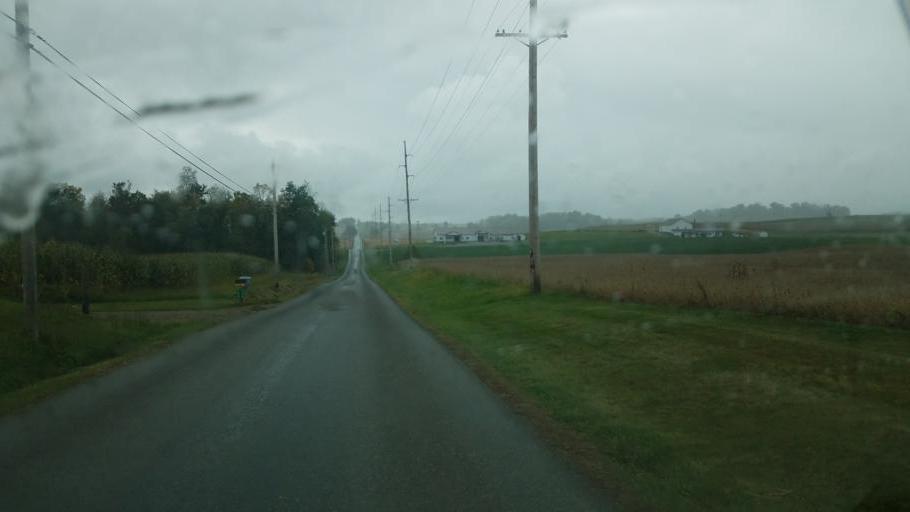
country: US
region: Ohio
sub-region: Holmes County
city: Millersburg
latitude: 40.5908
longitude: -81.8493
